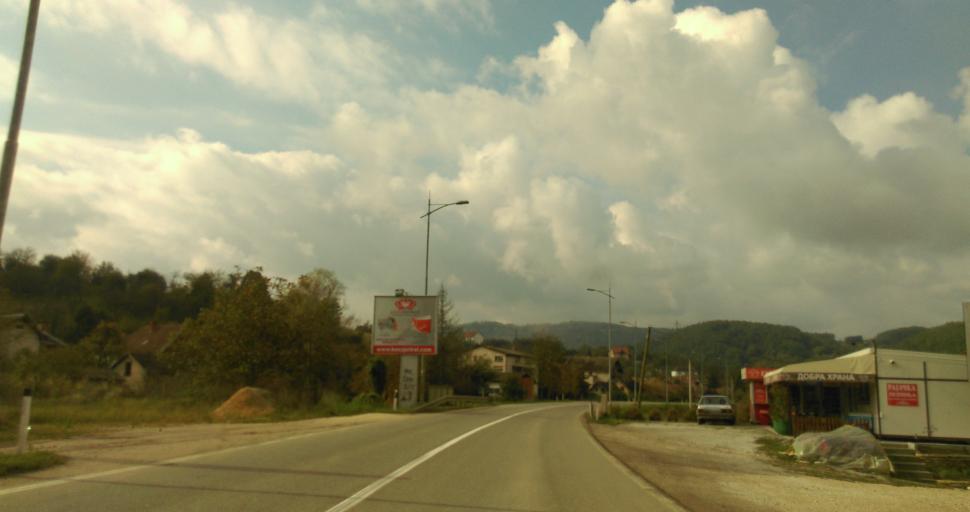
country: RS
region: Central Serbia
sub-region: Kolubarski Okrug
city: Ljig
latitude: 44.2223
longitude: 20.2353
